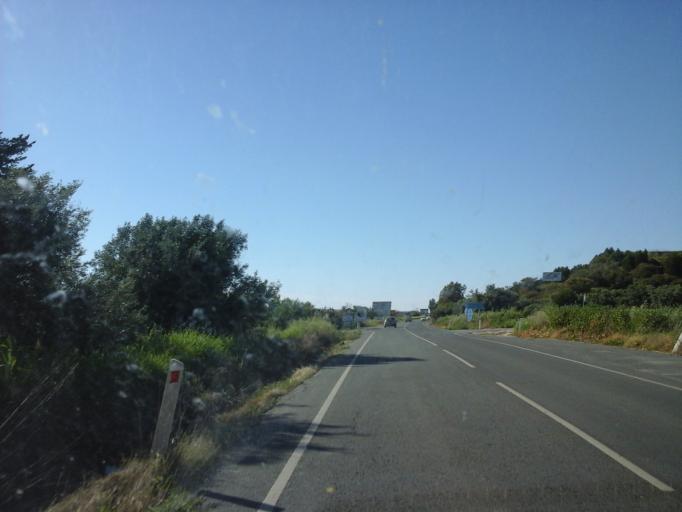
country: CY
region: Pafos
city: Polis
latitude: 35.0055
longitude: 32.4407
